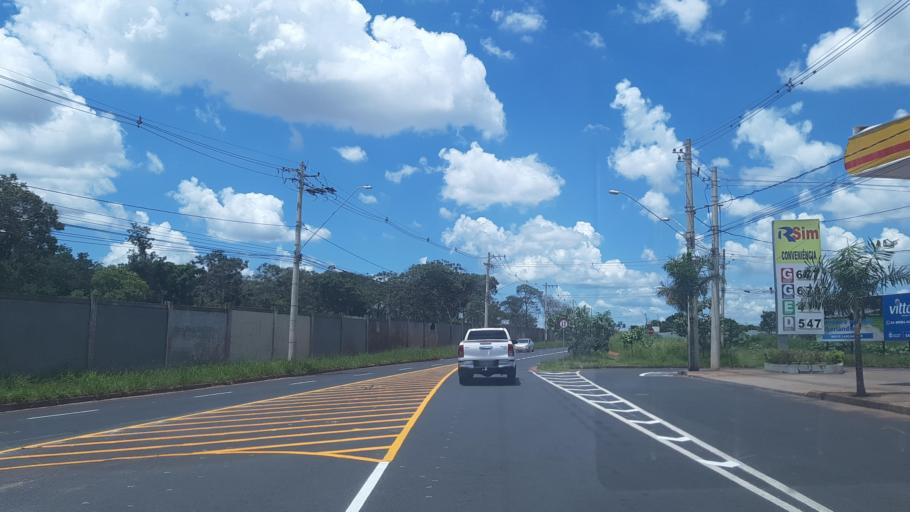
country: BR
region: Minas Gerais
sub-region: Uberlandia
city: Uberlandia
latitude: -18.9619
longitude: -48.3393
